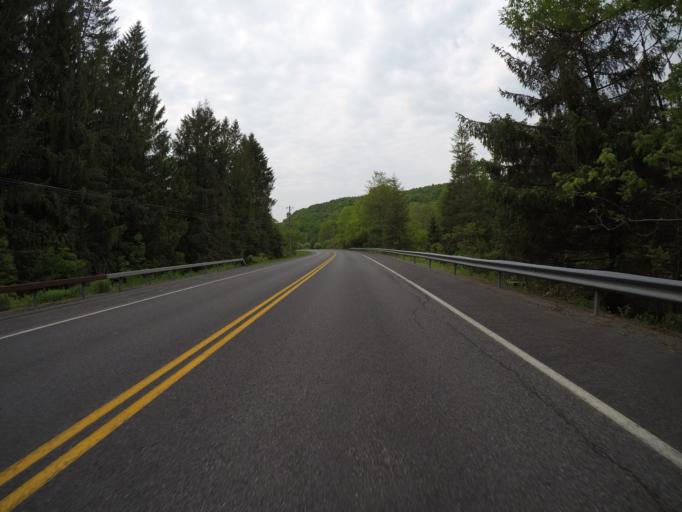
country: US
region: New York
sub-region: Sullivan County
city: Livingston Manor
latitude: 41.9864
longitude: -74.8944
